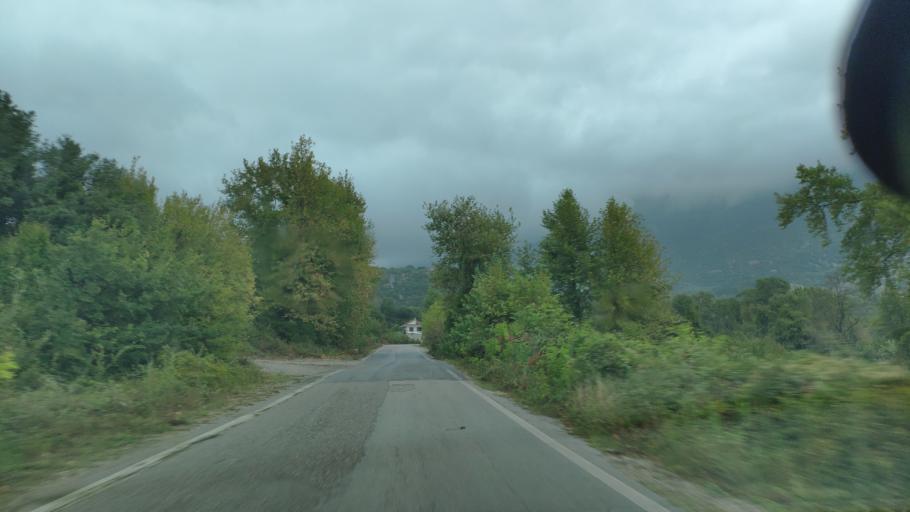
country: GR
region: West Greece
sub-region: Nomos Aitolias kai Akarnanias
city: Krikellos
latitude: 39.0171
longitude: 21.3075
